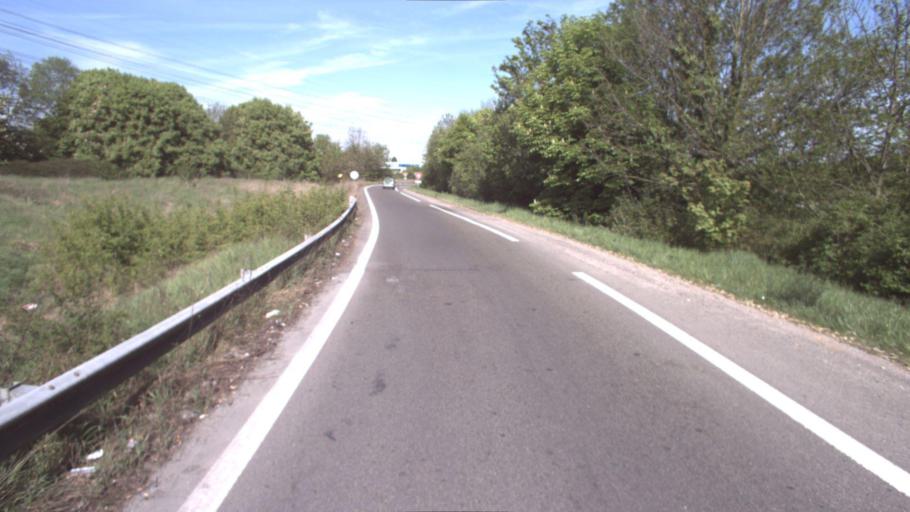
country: FR
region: Ile-de-France
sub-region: Departement de Seine-et-Marne
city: Collegien
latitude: 48.8430
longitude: 2.6646
